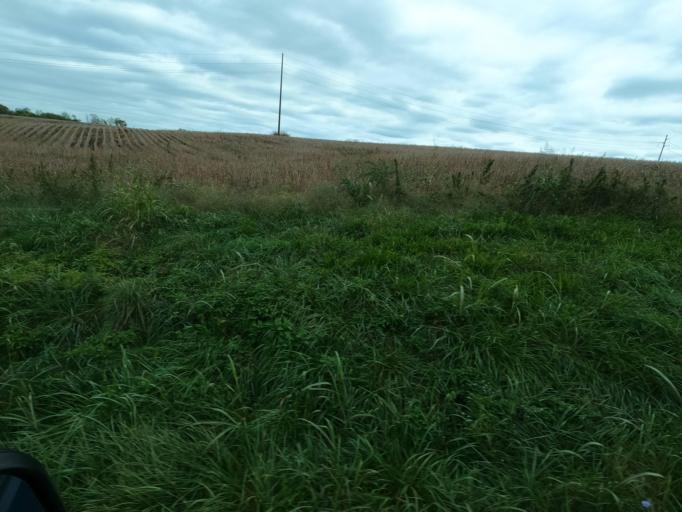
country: US
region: Tennessee
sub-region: Washington County
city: Jonesborough
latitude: 36.2350
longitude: -82.5821
